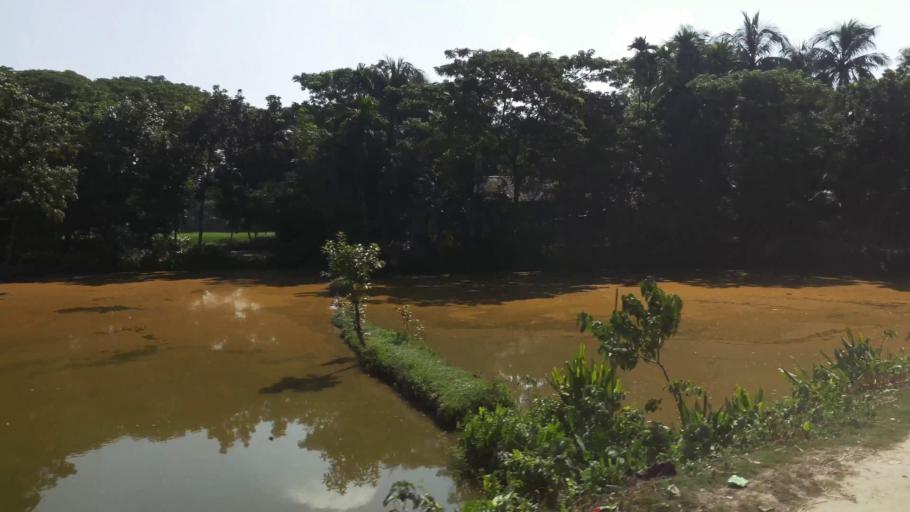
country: BD
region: Dhaka
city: Gafargaon
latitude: 24.4933
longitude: 90.5248
